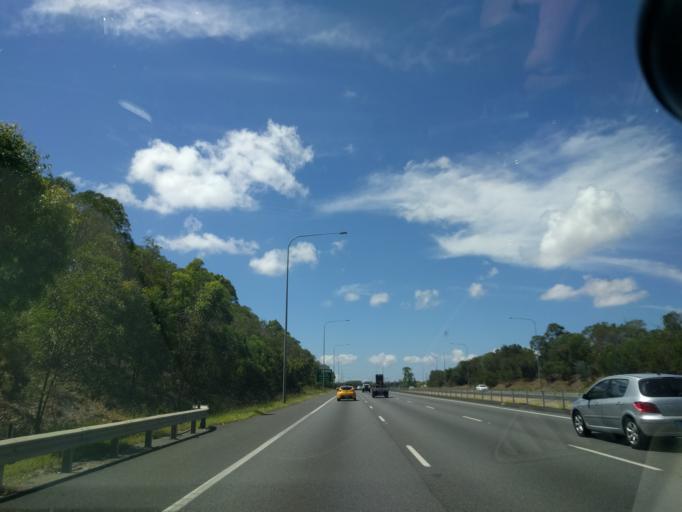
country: AU
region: Queensland
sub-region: Moreton Bay
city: Murrumba Downs
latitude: -27.2592
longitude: 153.0185
